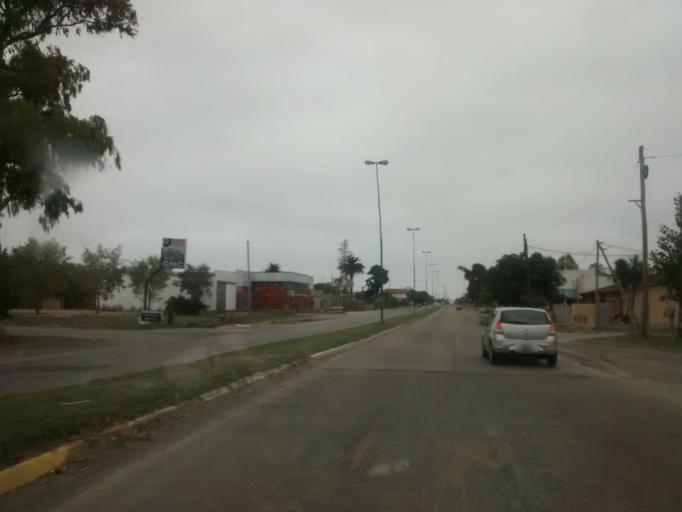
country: AR
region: Buenos Aires
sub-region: Partido de La Plata
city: La Plata
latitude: -34.9904
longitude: -58.0429
